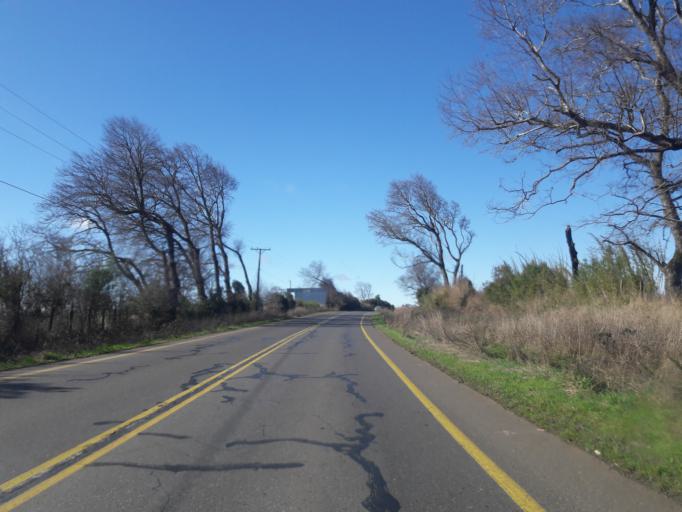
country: CL
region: Araucania
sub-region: Provincia de Malleco
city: Victoria
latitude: -38.2534
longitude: -72.2828
